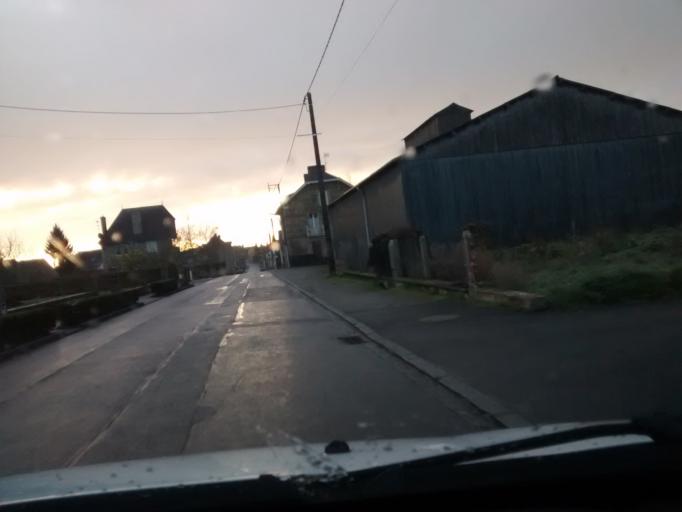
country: FR
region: Brittany
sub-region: Departement d'Ille-et-Vilaine
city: Bais
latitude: 48.0128
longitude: -1.2949
